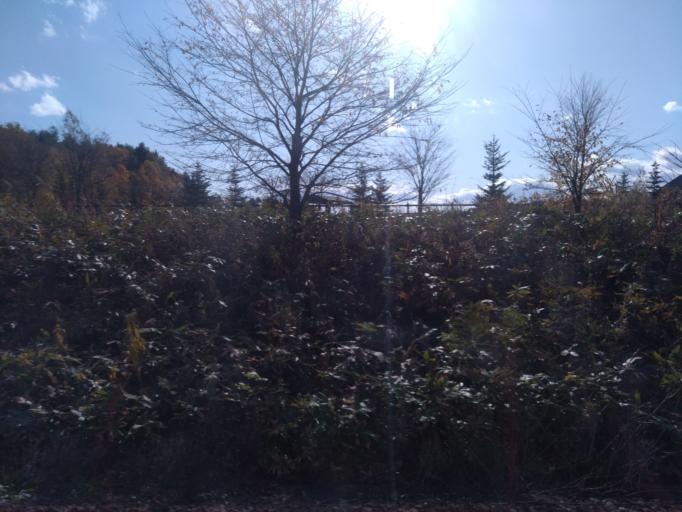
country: JP
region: Hokkaido
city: Kitahiroshima
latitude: 42.9998
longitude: 141.5253
